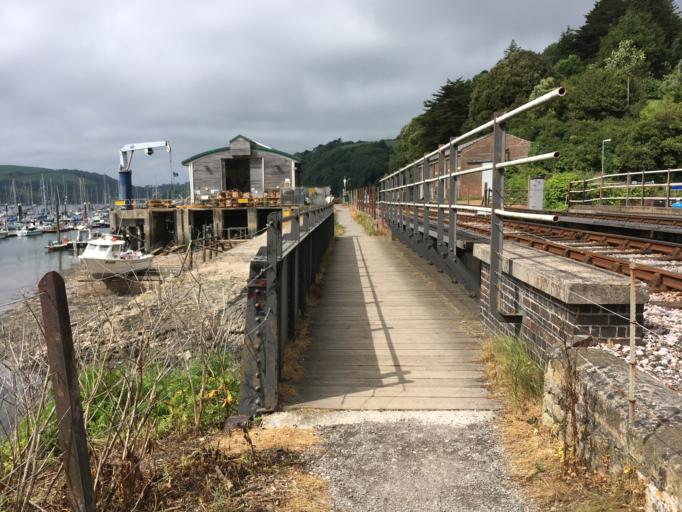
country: GB
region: England
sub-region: Devon
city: Dartmouth
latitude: 50.3512
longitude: -3.5703
